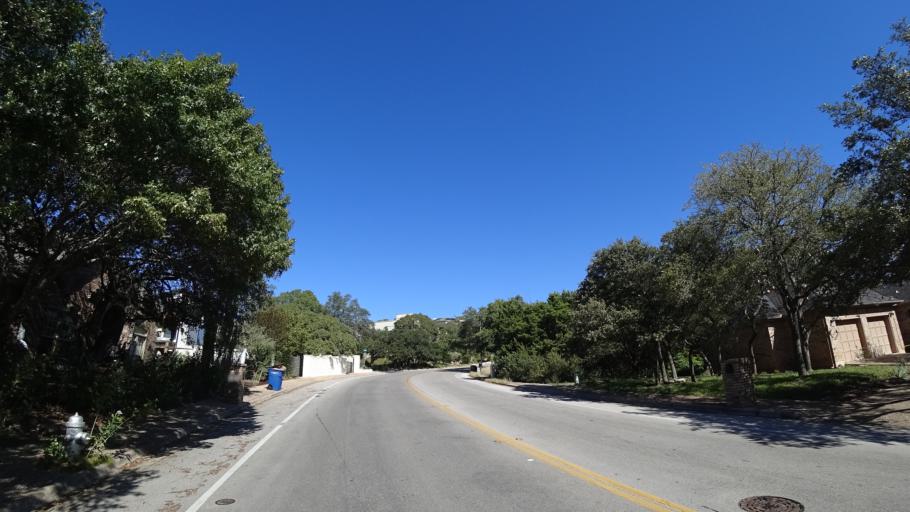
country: US
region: Texas
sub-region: Travis County
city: West Lake Hills
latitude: 30.3483
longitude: -97.7720
